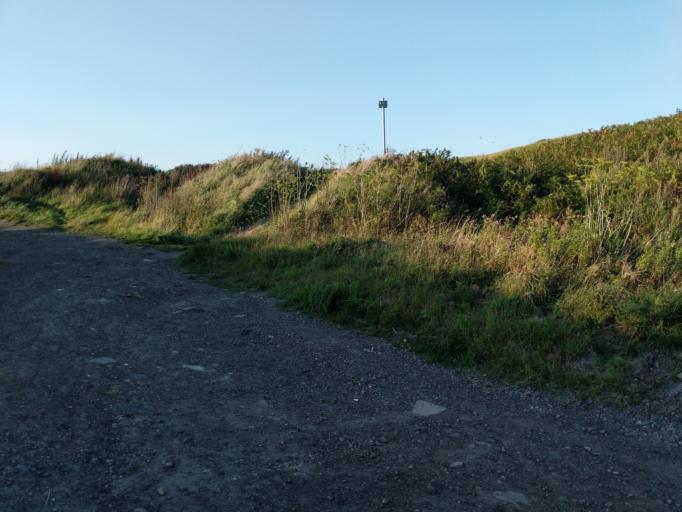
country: GB
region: England
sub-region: Northumberland
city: Lynemouth
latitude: 55.2199
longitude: -1.5299
